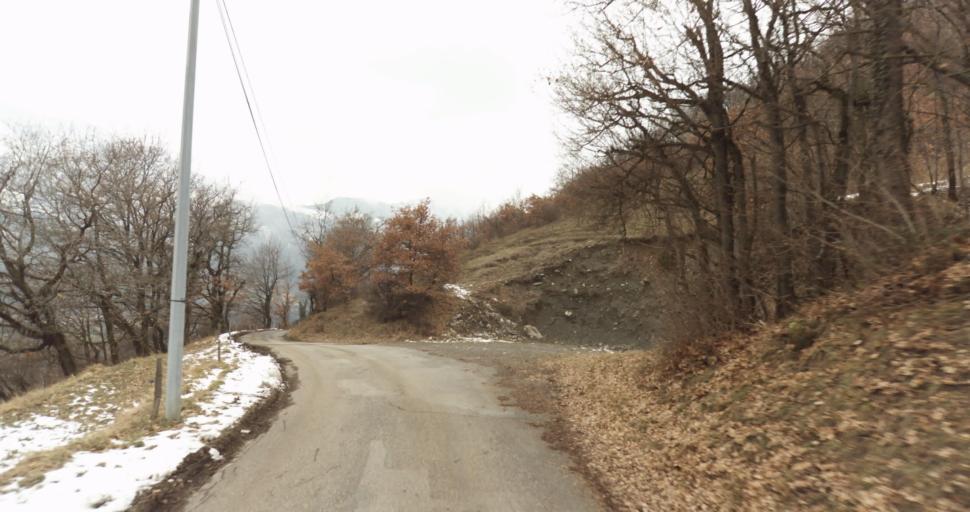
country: FR
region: Rhone-Alpes
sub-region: Departement de l'Isere
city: Vif
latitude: 45.0193
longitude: 5.6650
